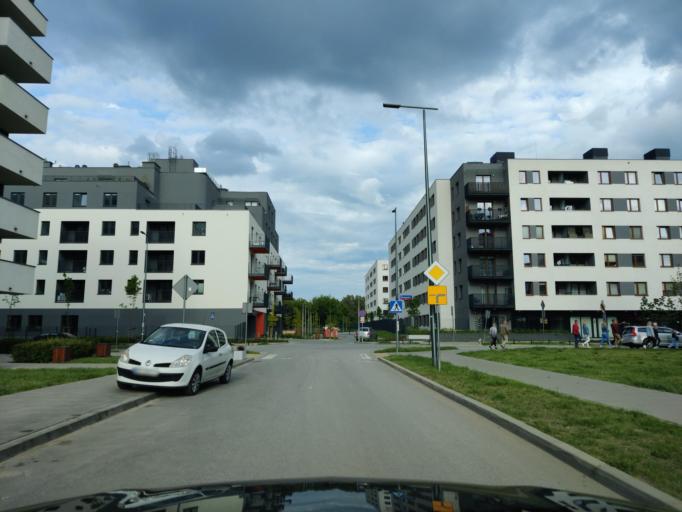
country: PL
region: Masovian Voivodeship
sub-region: Warszawa
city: Praga Poludnie
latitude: 52.2547
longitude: 21.0810
